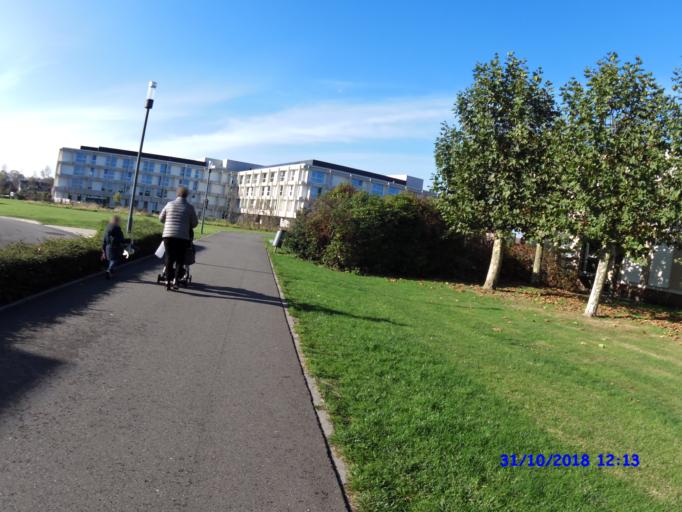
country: BE
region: Flanders
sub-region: Provincie Antwerpen
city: Turnhout
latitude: 51.3147
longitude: 4.9414
